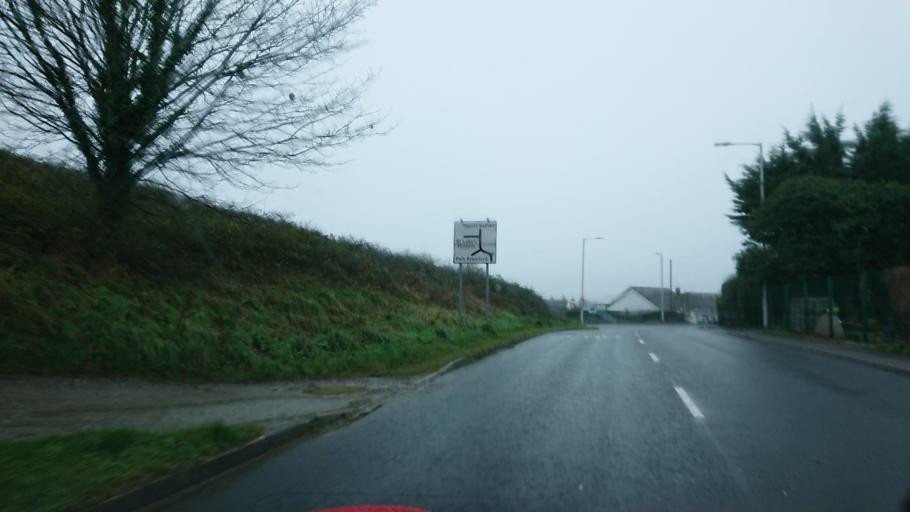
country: GB
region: England
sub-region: Plymouth
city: Plymstock
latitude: 50.3558
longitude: -4.1175
